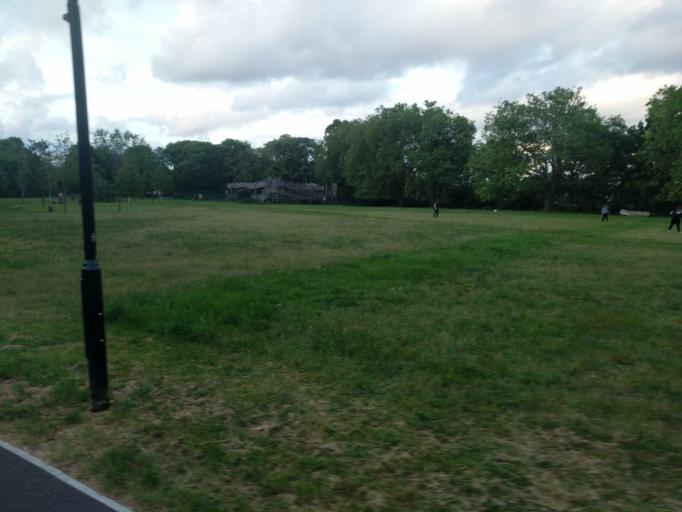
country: GB
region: England
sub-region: Greater London
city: Catford
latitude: 51.4502
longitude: -0.0242
